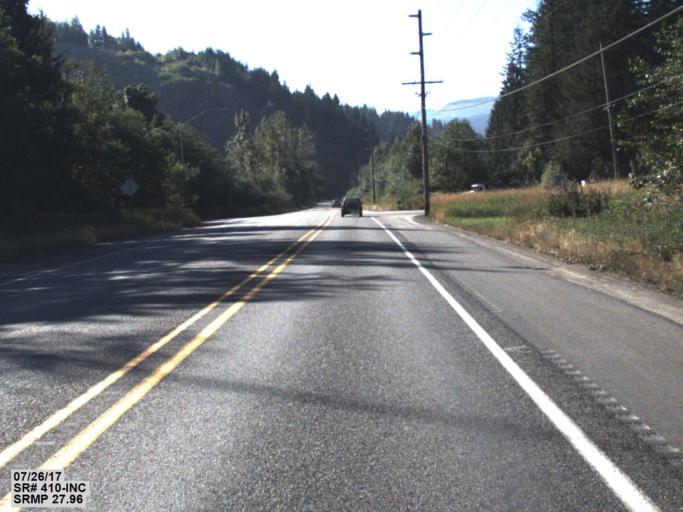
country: US
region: Washington
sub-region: King County
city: Enumclaw
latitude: 47.1833
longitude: -121.9244
